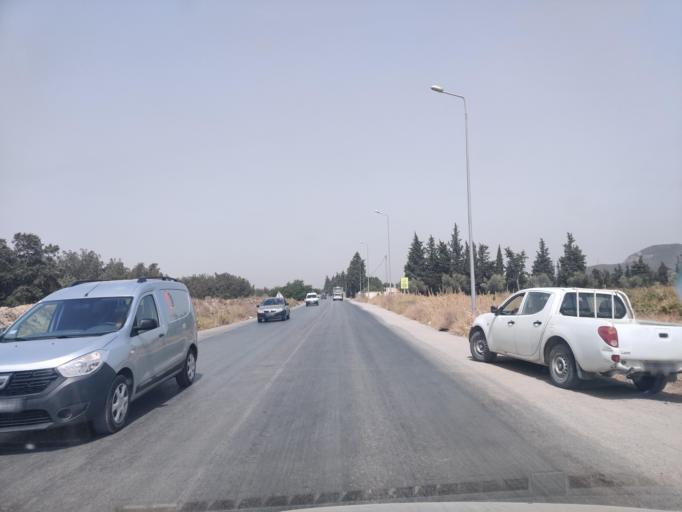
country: TN
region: Tunis
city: La Sebala du Mornag
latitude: 36.6750
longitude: 10.3169
